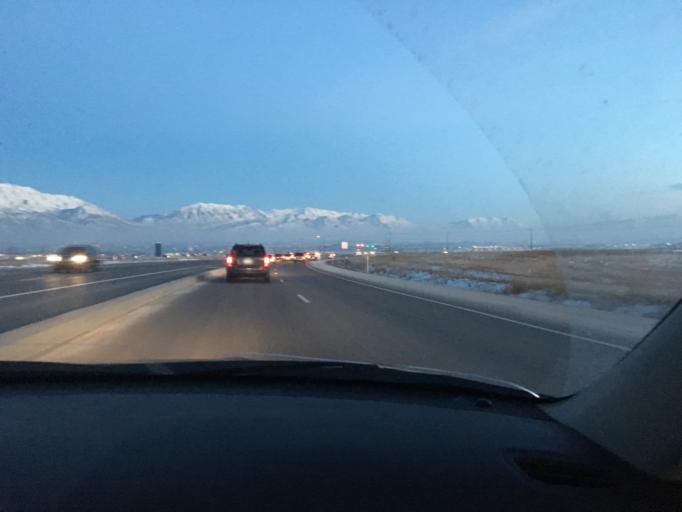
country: US
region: Utah
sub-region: Utah County
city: Saratoga Springs
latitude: 40.3858
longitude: -111.9346
